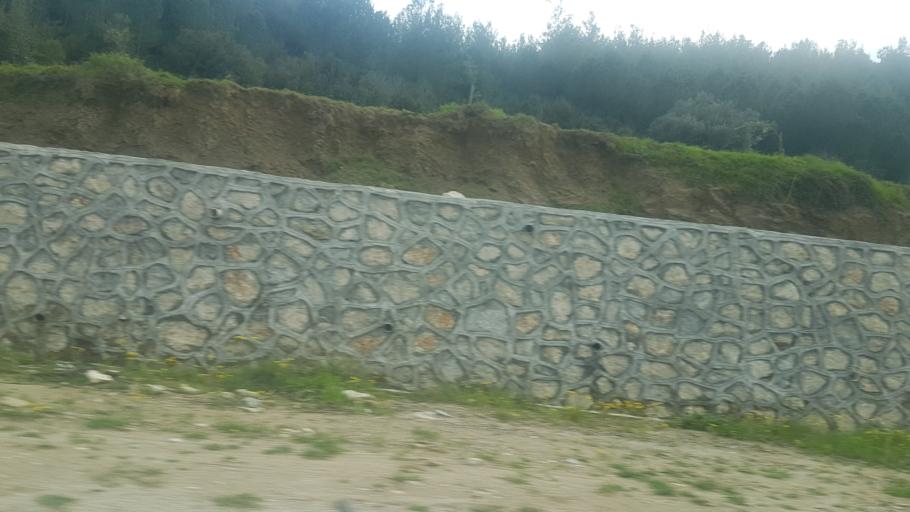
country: TR
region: Mersin
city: Yenice
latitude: 37.0896
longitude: 35.1558
